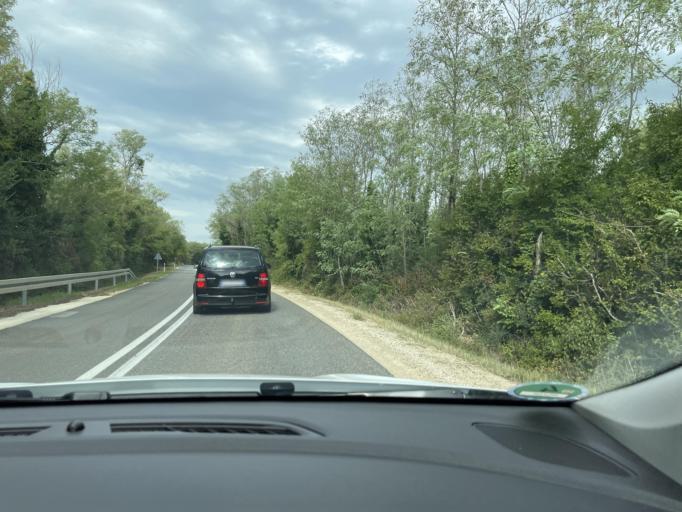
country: HR
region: Istarska
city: Vrsar
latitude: 45.2017
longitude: 13.6993
